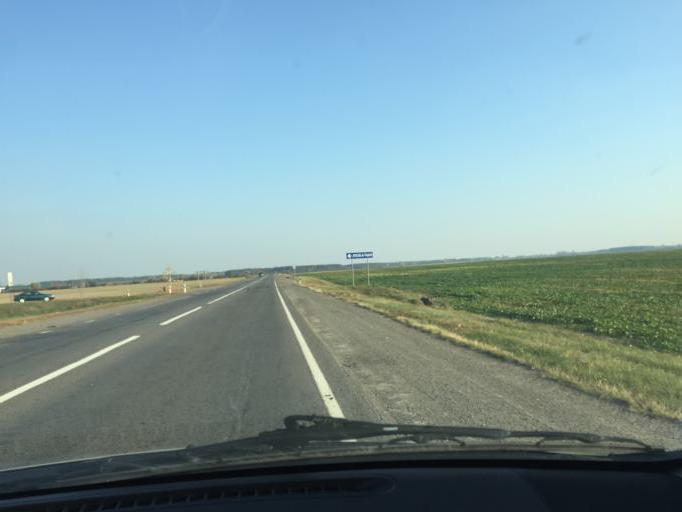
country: BY
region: Brest
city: Luninyets
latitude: 52.2537
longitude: 27.0546
